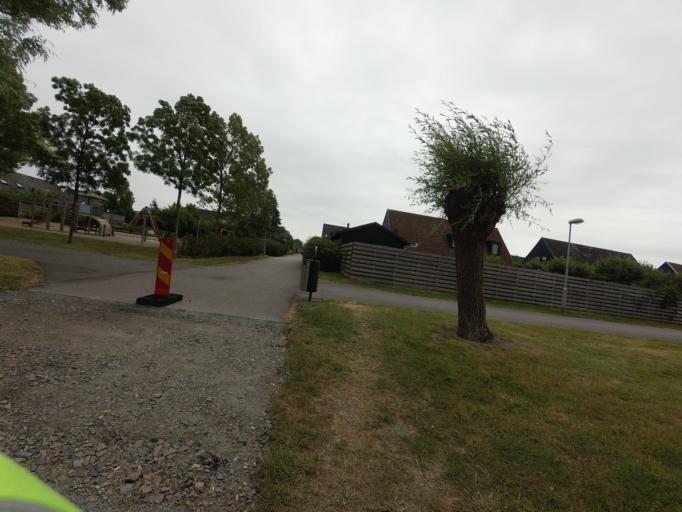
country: SE
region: Skane
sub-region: Malmo
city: Bunkeflostrand
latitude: 55.5477
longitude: 12.9132
